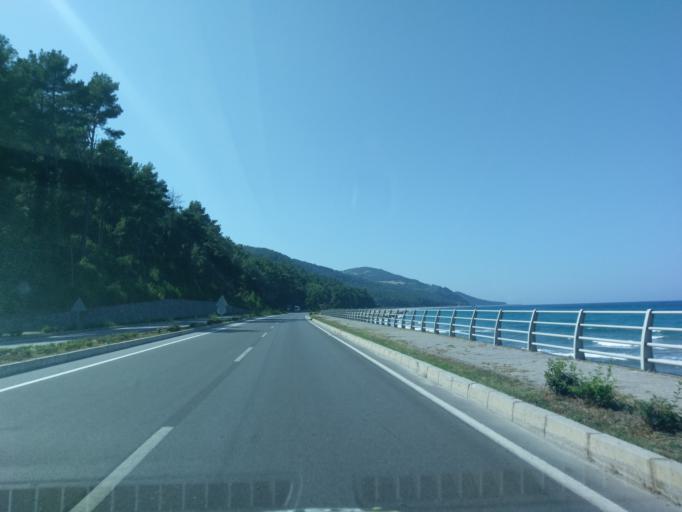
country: TR
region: Samsun
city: Yakakent
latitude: 41.6459
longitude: 35.4730
